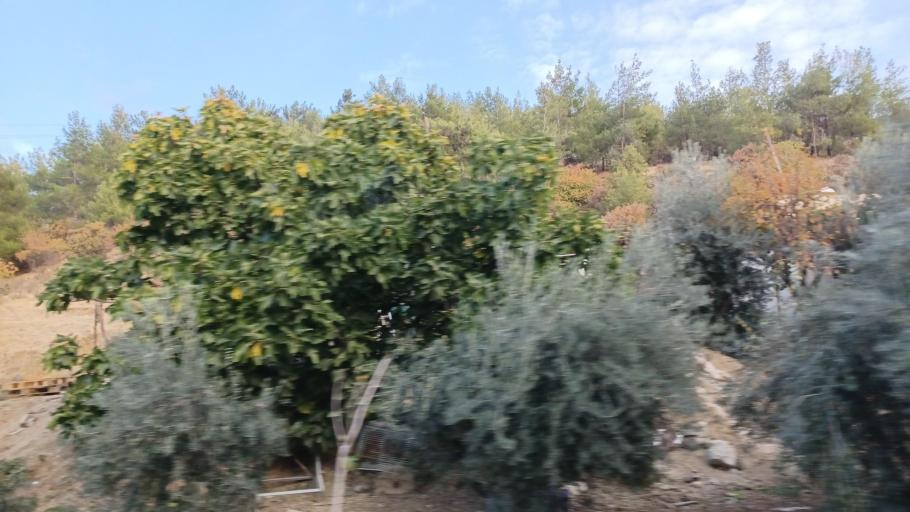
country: CY
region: Lefkosia
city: Kakopetria
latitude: 35.0225
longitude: 32.8991
